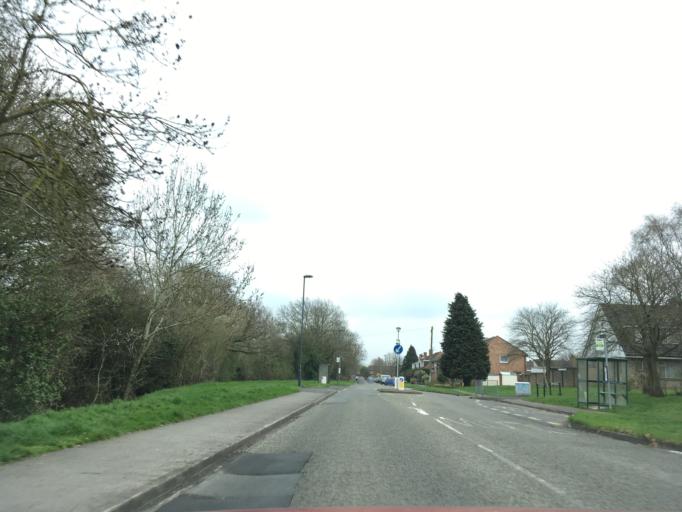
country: GB
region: England
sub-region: South Gloucestershire
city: Stoke Gifford
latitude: 51.5320
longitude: -2.5566
